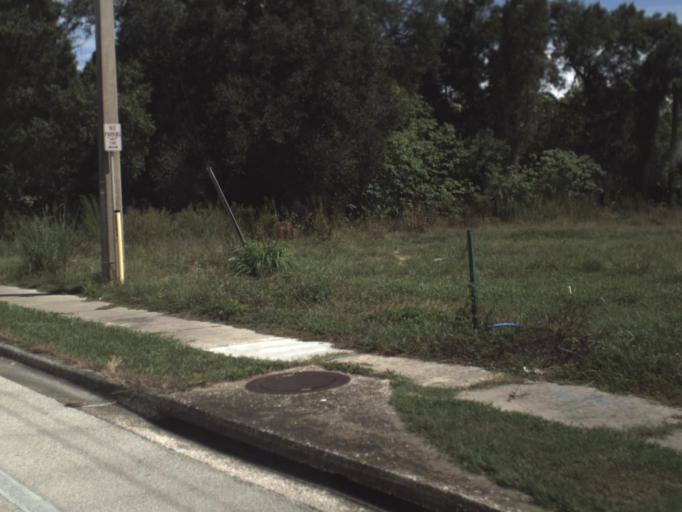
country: US
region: Florida
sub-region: Polk County
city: Mulberry
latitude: 27.8949
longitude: -81.9644
